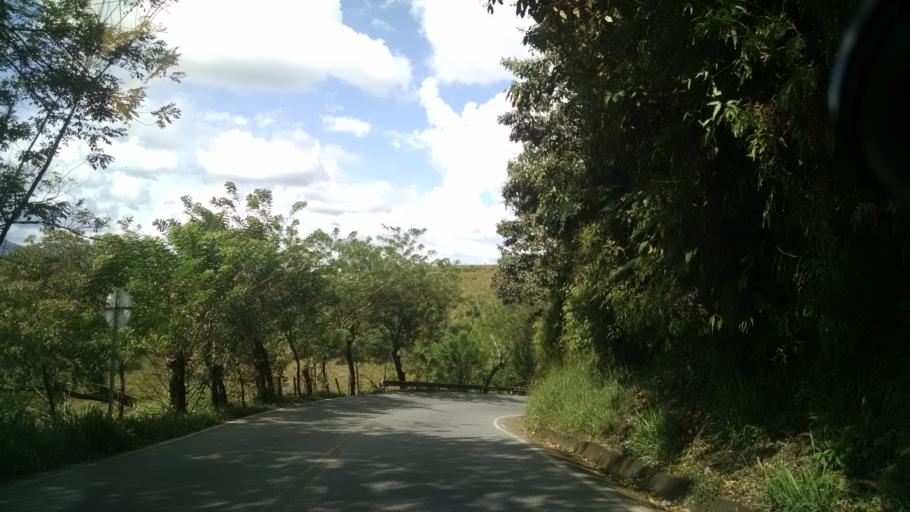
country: CO
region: Antioquia
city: Santo Domingo
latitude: 6.5337
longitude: -75.2336
